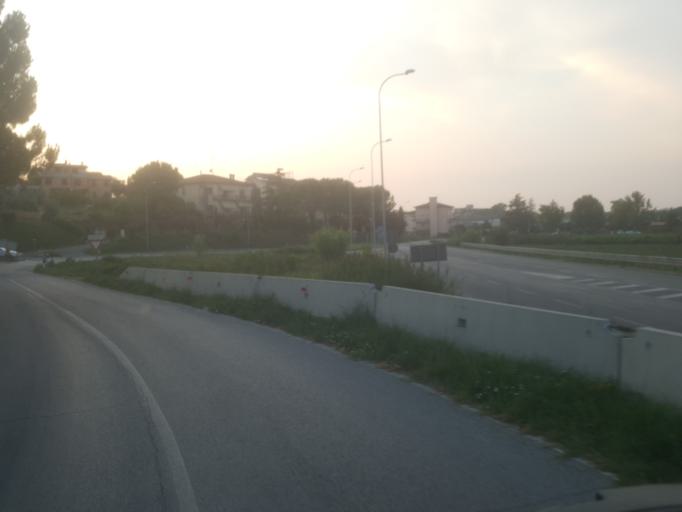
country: IT
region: Tuscany
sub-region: Province of Florence
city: Certaldo
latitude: 43.5386
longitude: 11.0346
